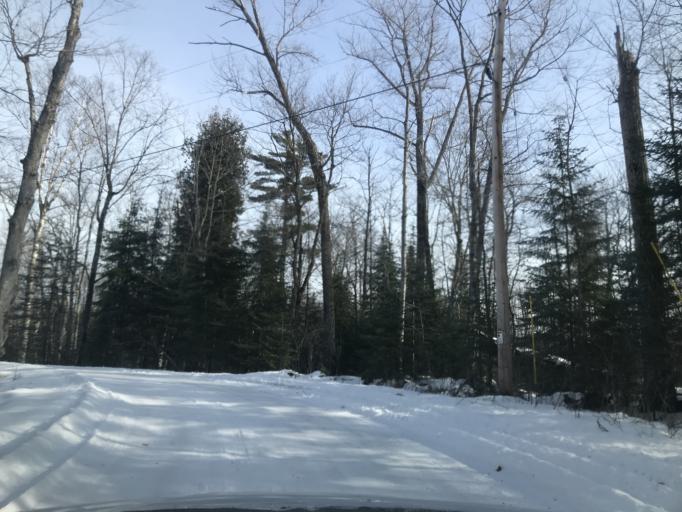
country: US
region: Wisconsin
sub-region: Door County
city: Sturgeon Bay
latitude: 45.1543
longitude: -87.0492
